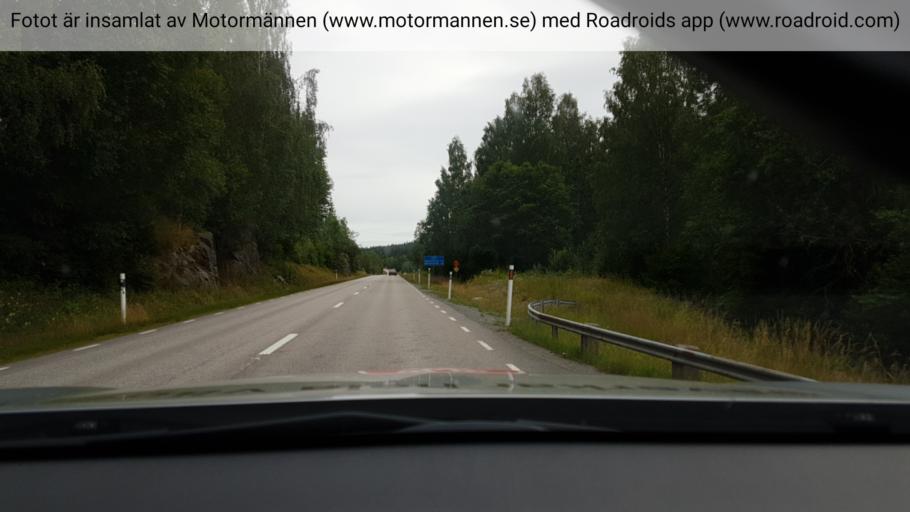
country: SE
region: Vaestra Goetaland
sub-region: Bengtsfors Kommun
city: Billingsfors
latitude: 58.9391
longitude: 12.2124
